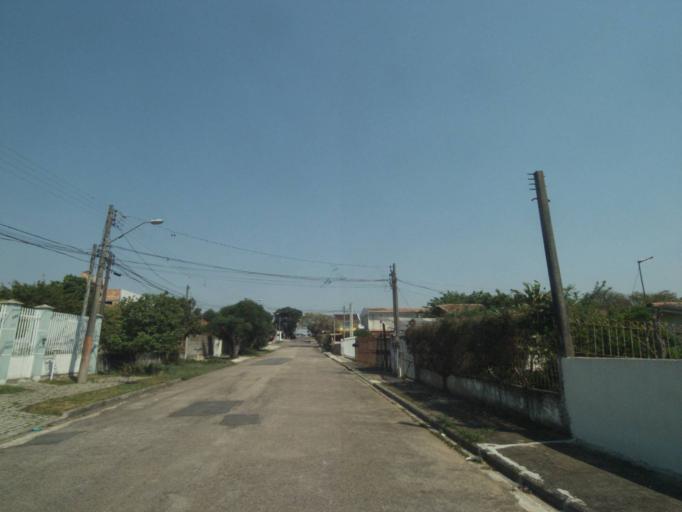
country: BR
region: Parana
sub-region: Sao Jose Dos Pinhais
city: Sao Jose dos Pinhais
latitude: -25.5103
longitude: -49.2686
